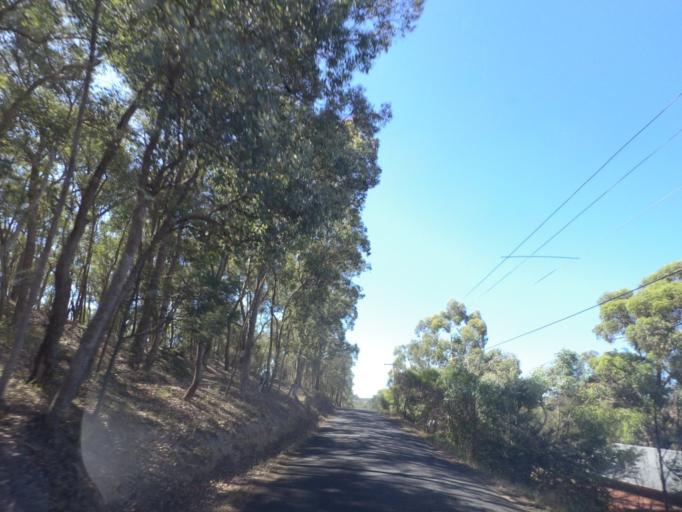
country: AU
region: Victoria
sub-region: Yarra Ranges
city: Chirnside Park
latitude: -37.7216
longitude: 145.2854
